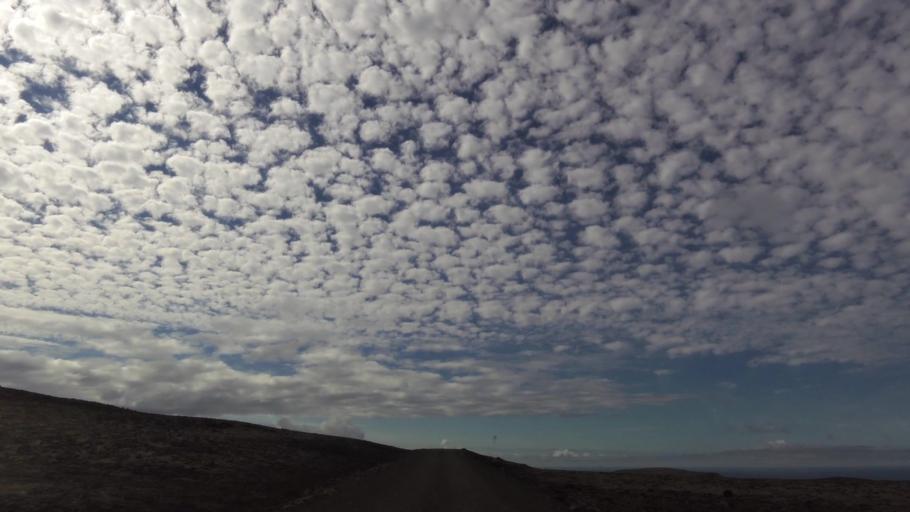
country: IS
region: West
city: Olafsvik
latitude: 65.6194
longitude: -24.2654
